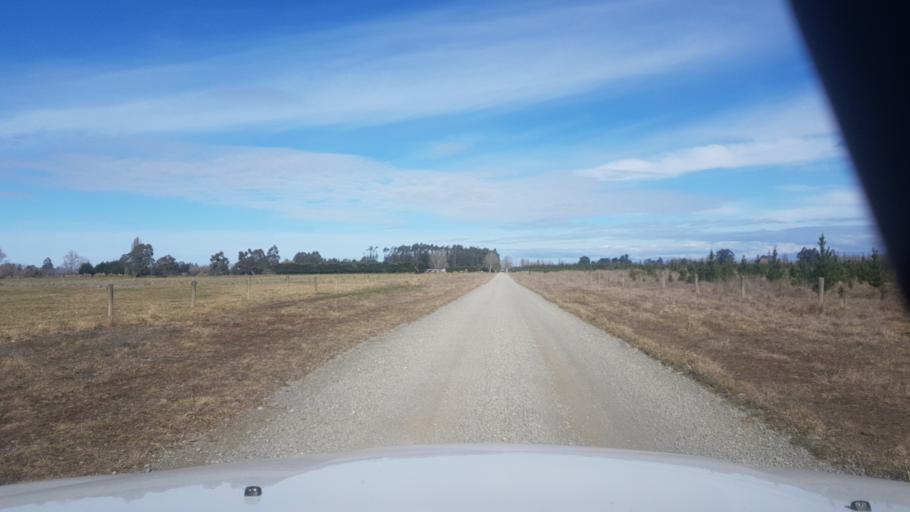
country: NZ
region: Canterbury
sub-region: Timaru District
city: Pleasant Point
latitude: -44.1319
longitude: 171.2793
